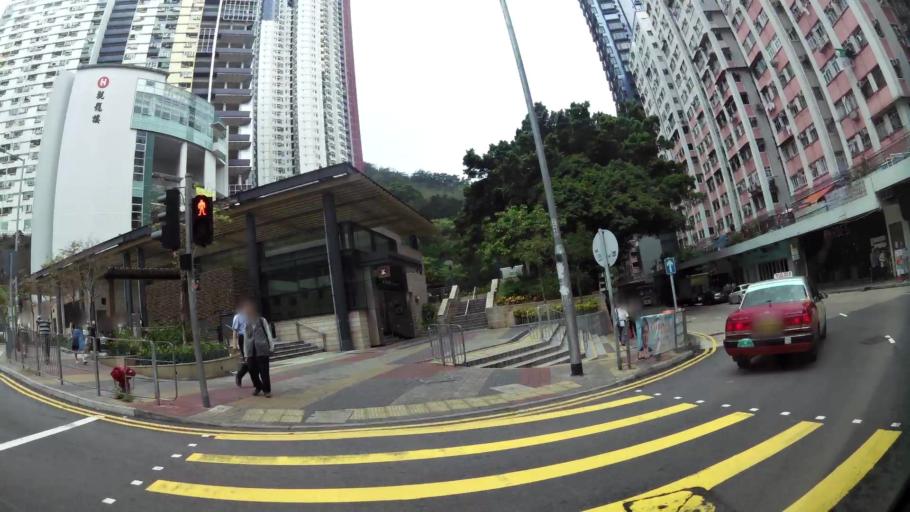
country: HK
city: Hong Kong
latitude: 22.2815
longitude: 114.1282
